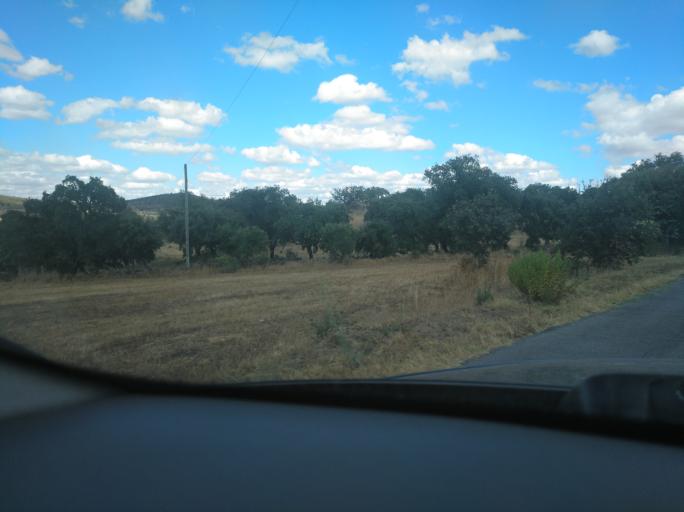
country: ES
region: Extremadura
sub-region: Provincia de Badajoz
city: La Codosera
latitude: 39.1536
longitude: -7.1646
